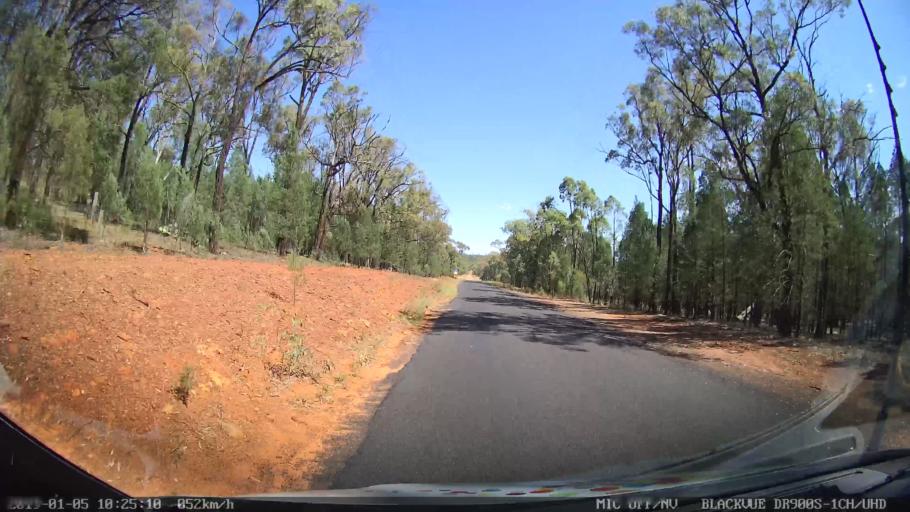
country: AU
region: New South Wales
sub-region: Gilgandra
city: Gilgandra
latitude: -31.5634
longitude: 148.9607
